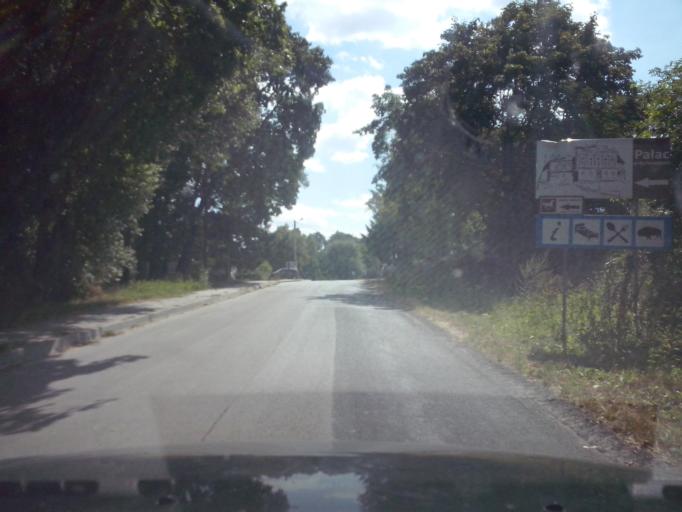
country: PL
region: Swietokrzyskie
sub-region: Powiat staszowski
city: Staszow
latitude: 50.5944
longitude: 21.0957
